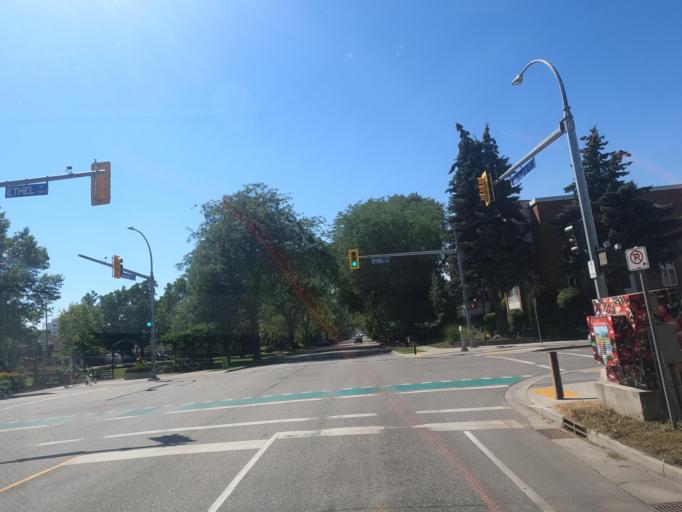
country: CA
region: British Columbia
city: Kelowna
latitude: 49.8864
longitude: -119.4826
